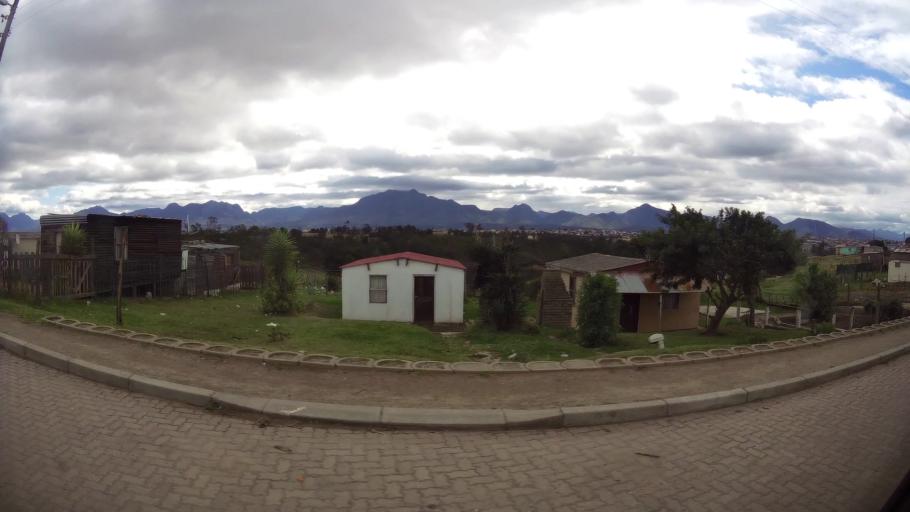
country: ZA
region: Western Cape
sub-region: Eden District Municipality
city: George
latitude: -34.0160
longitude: 22.4716
